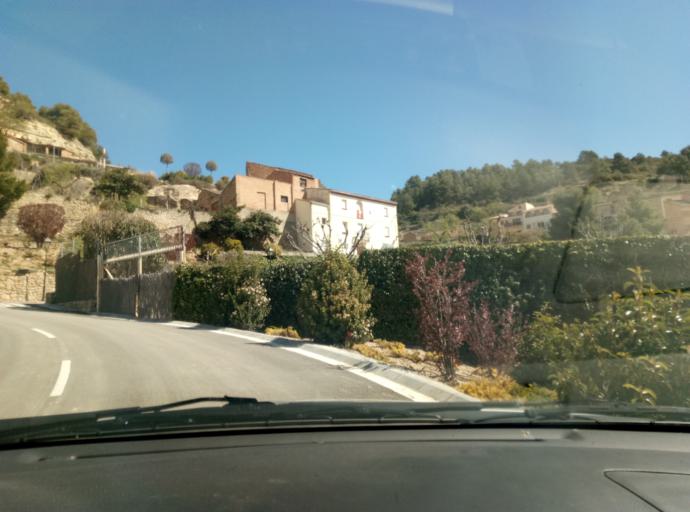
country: ES
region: Catalonia
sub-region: Provincia de Lleida
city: Vallbona de les Monges
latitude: 41.5269
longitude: 1.0874
